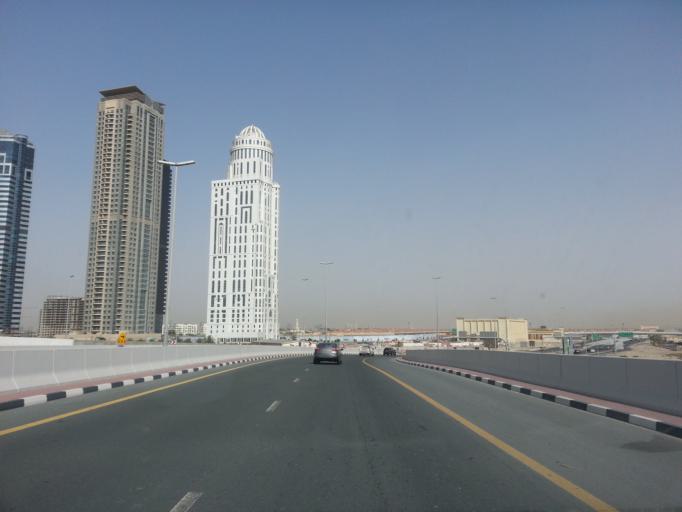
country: AE
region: Dubai
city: Dubai
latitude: 25.0635
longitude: 55.1335
